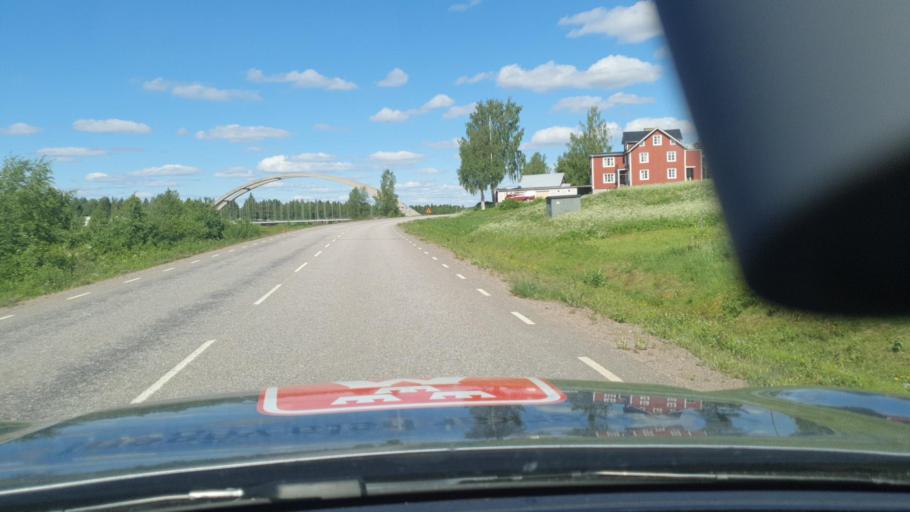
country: SE
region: Norrbotten
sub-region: Pajala Kommun
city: Pajala
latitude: 67.1658
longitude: 22.6173
